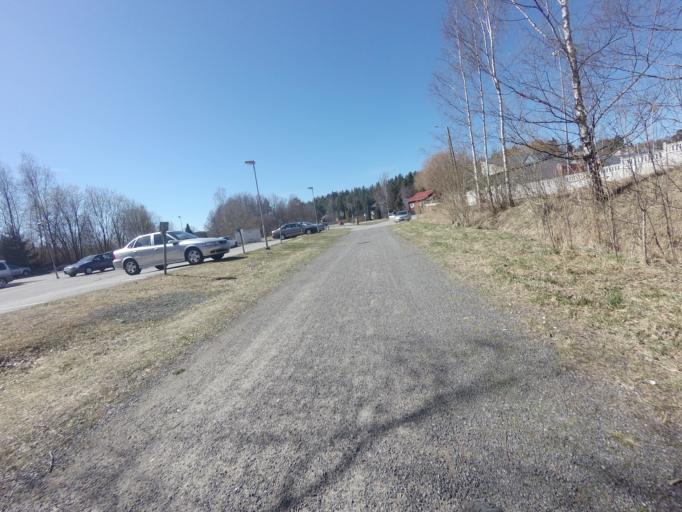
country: FI
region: Varsinais-Suomi
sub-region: Turku
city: Raisio
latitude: 60.4549
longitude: 22.1717
